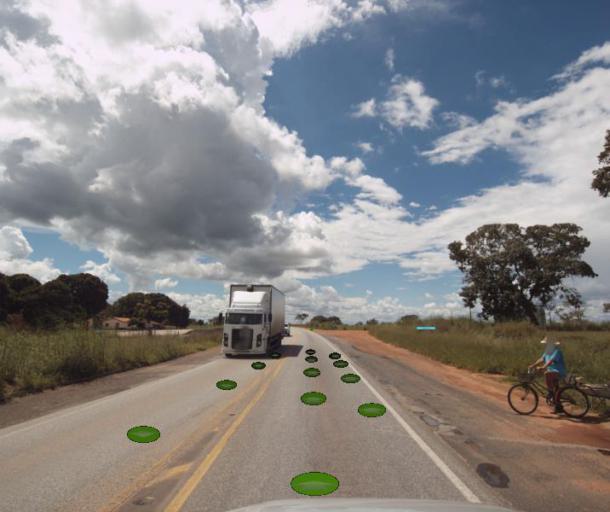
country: BR
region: Goias
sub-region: Uruacu
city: Uruacu
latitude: -14.0128
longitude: -49.0855
